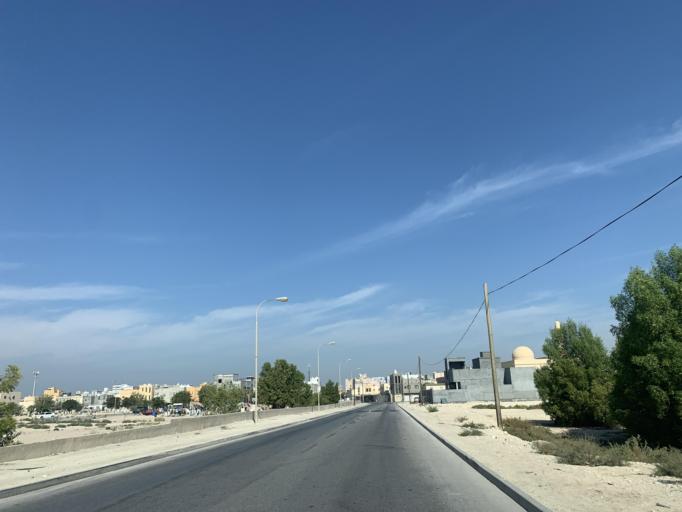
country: BH
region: Central Governorate
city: Madinat Hamad
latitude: 26.1141
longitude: 50.4861
